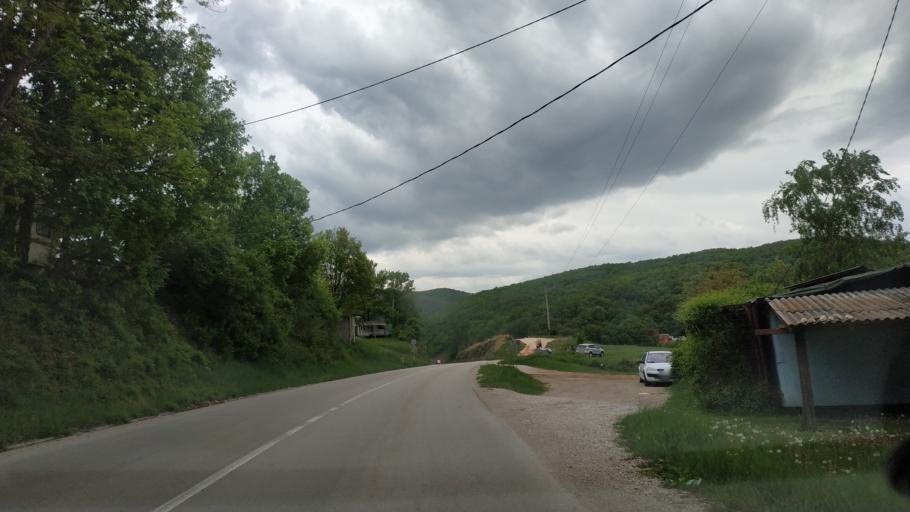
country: RS
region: Central Serbia
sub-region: Nisavski Okrug
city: Aleksinac
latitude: 43.6428
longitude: 21.7137
